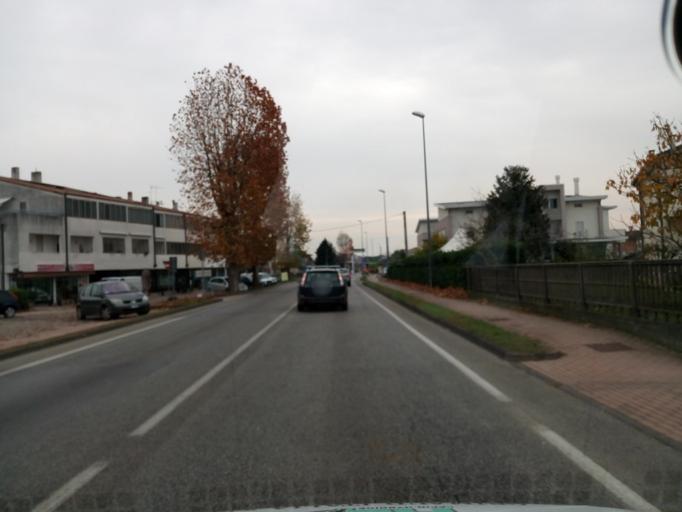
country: IT
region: Veneto
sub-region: Provincia di Treviso
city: Falze-Signoressa
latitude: 45.7508
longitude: 12.1046
